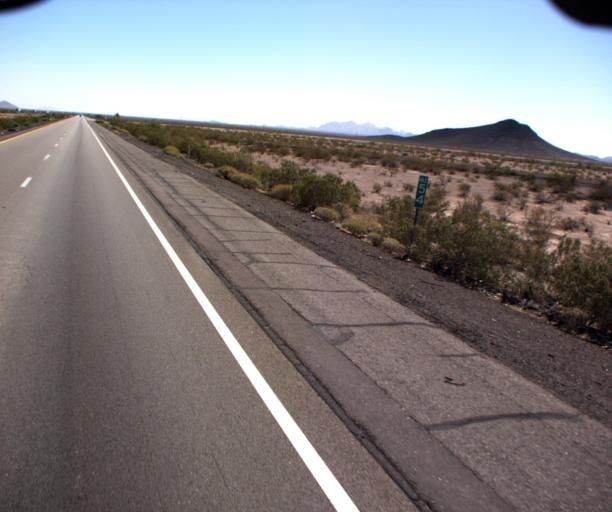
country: US
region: Arizona
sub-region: La Paz County
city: Salome
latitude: 33.6087
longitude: -113.6192
